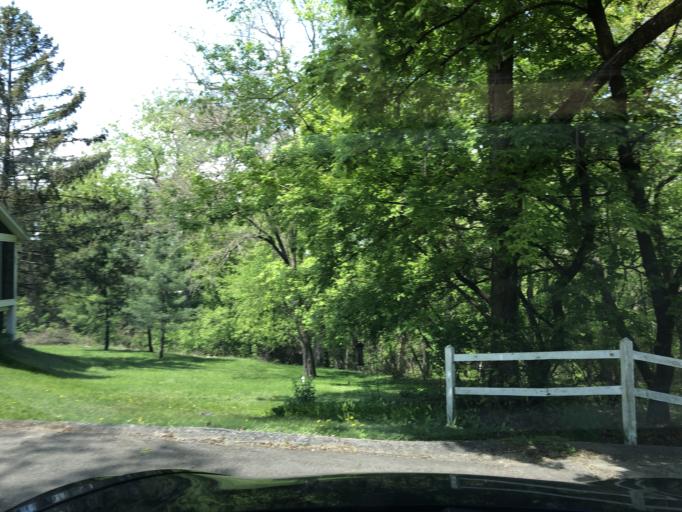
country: US
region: Iowa
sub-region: Dubuque County
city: Dubuque
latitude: 42.4819
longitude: -90.6630
